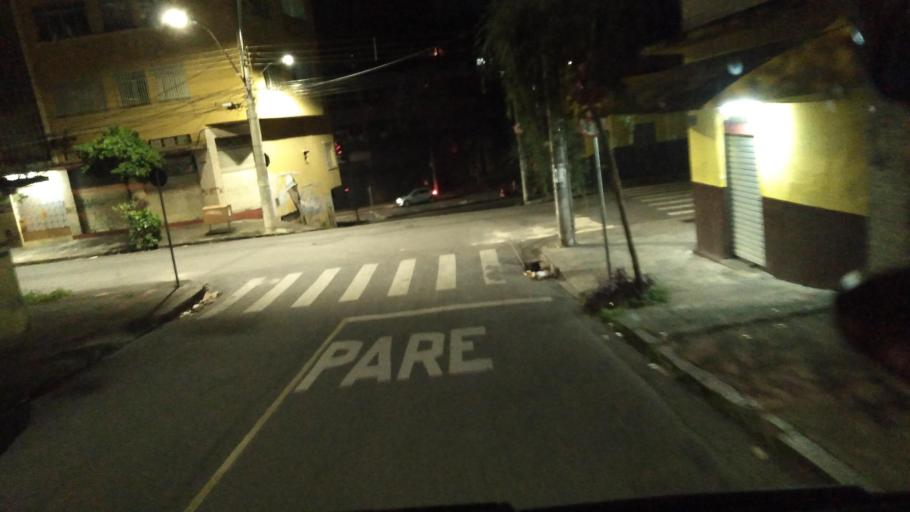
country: BR
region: Minas Gerais
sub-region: Belo Horizonte
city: Belo Horizonte
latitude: -19.9099
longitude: -43.9155
